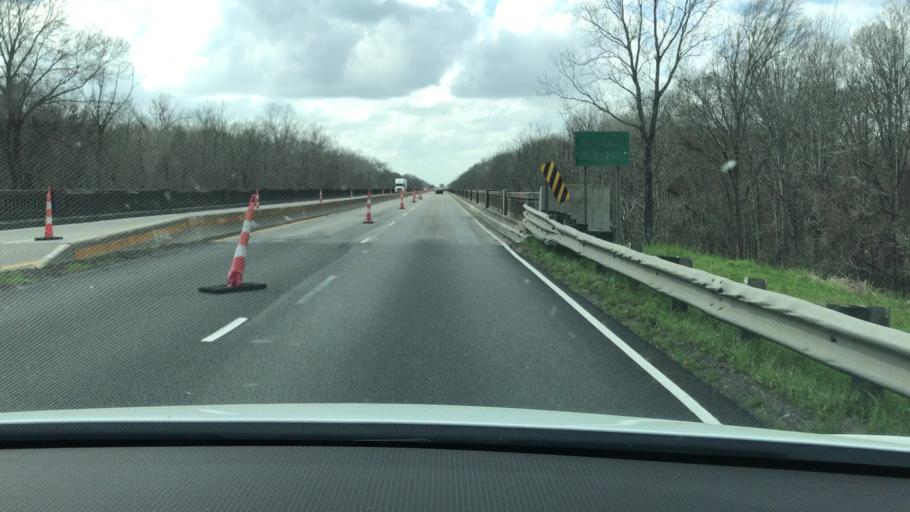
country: US
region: Louisiana
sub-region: Saint Landry Parish
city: Krotz Springs
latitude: 30.5563
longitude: -91.6651
